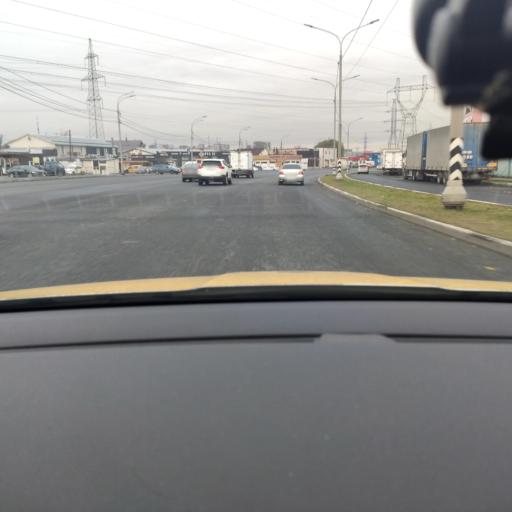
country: RU
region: Moskovskaya
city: Mosrentgen
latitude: 55.6237
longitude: 37.4420
